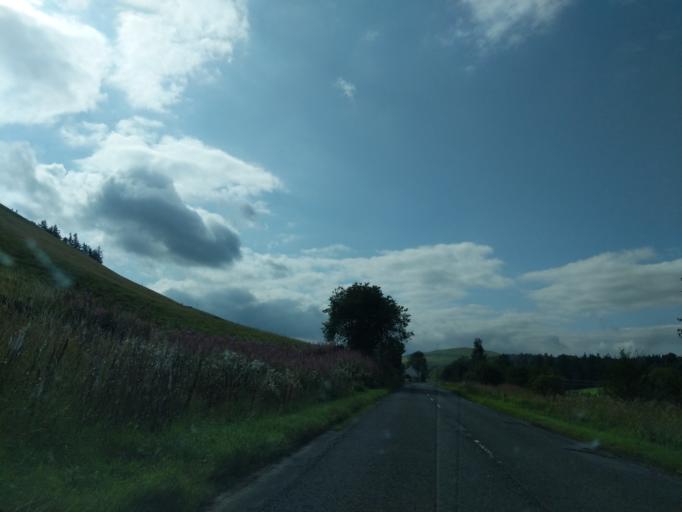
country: GB
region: Scotland
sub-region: The Scottish Borders
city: Peebles
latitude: 55.6943
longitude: -3.2129
